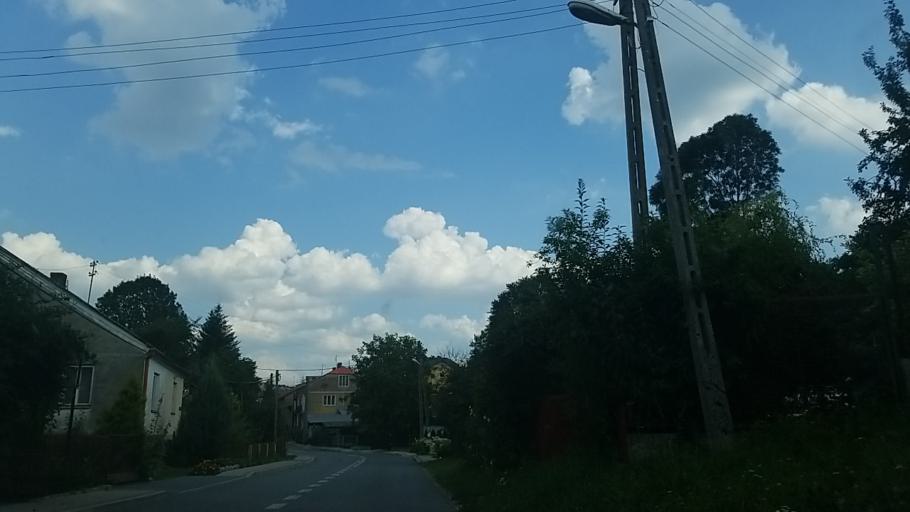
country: PL
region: Lublin Voivodeship
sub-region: Powiat bilgorajski
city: Goraj
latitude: 50.7220
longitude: 22.6632
